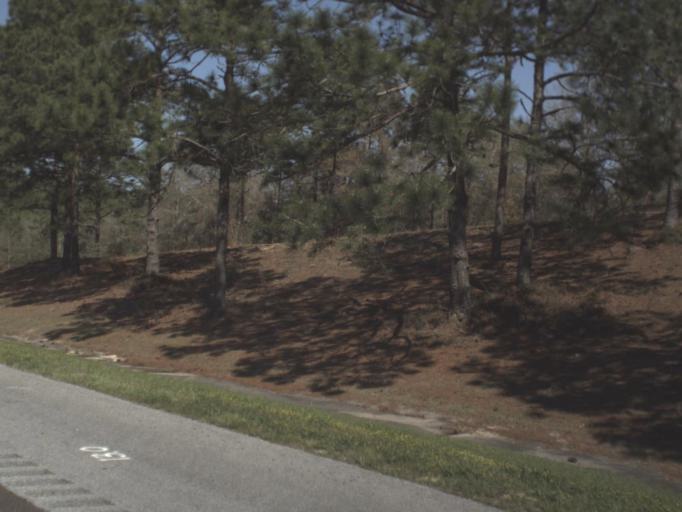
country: US
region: Florida
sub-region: Walton County
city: DeFuniak Springs
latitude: 30.7225
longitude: -86.1881
